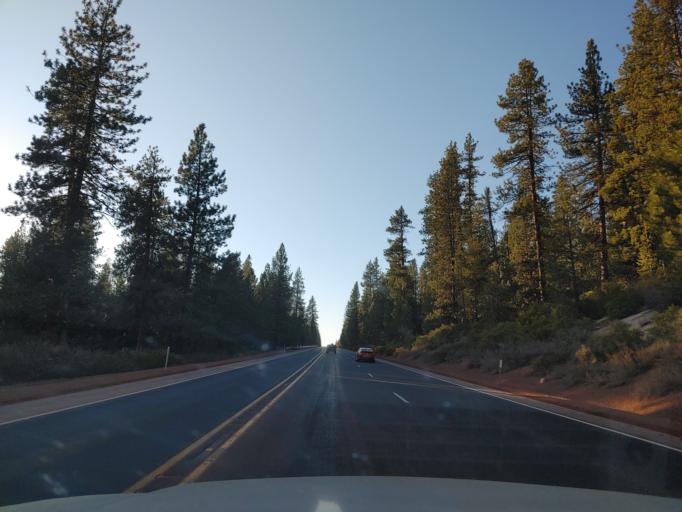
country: US
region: Oregon
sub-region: Deschutes County
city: La Pine
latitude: 43.4518
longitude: -121.8713
